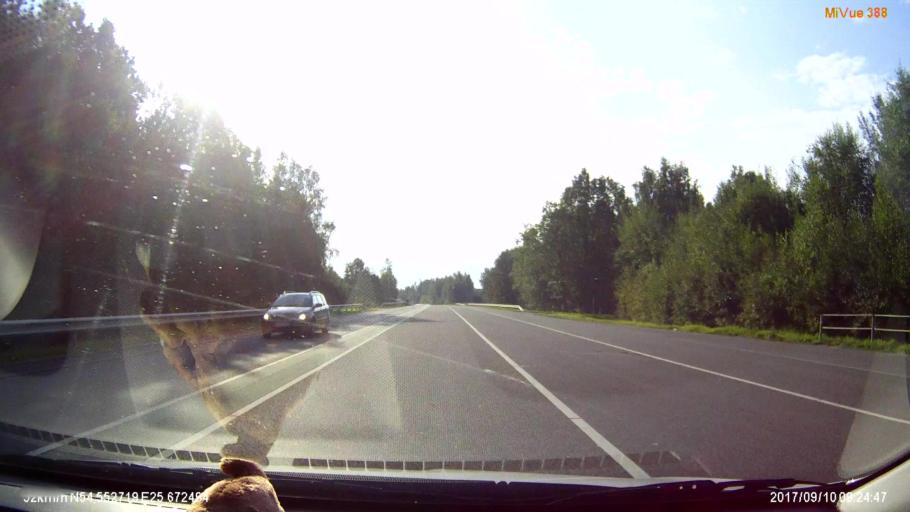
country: BY
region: Grodnenskaya
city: Astravyets
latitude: 54.5525
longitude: 25.6728
